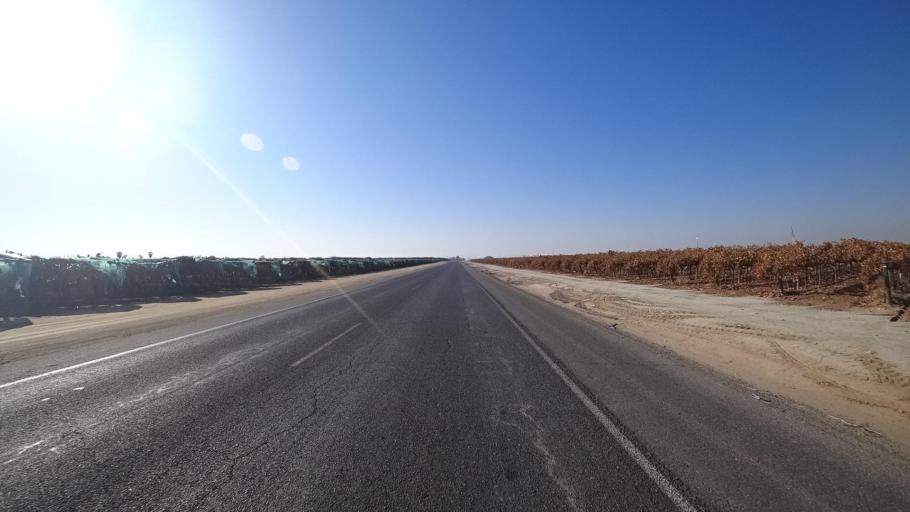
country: US
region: California
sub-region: Tulare County
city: Richgrove
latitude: 35.7535
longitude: -119.1378
